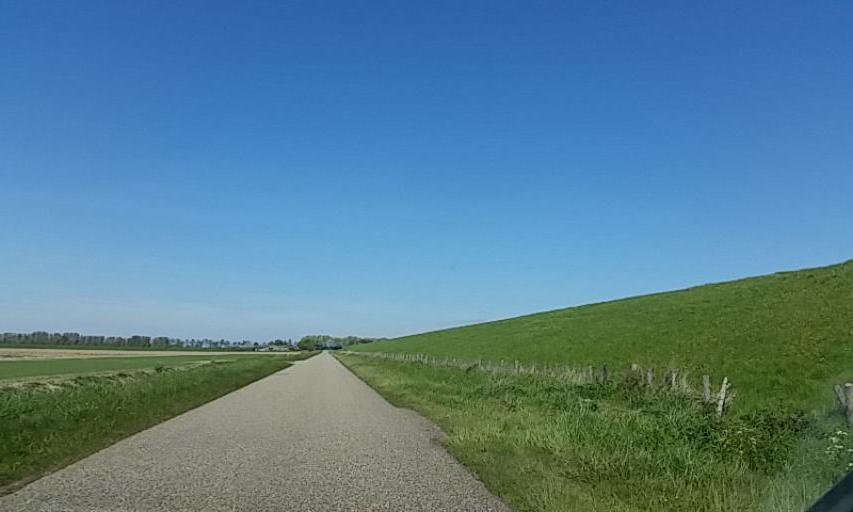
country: NL
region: Zeeland
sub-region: Gemeente Borsele
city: Borssele
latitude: 51.3587
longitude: 3.7017
